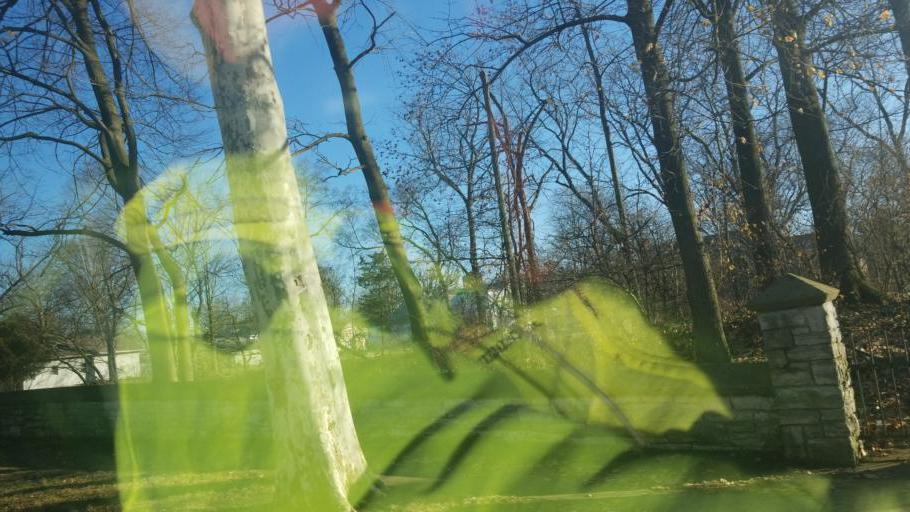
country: US
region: Ohio
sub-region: Marion County
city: Marion
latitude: 40.5840
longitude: -83.1199
